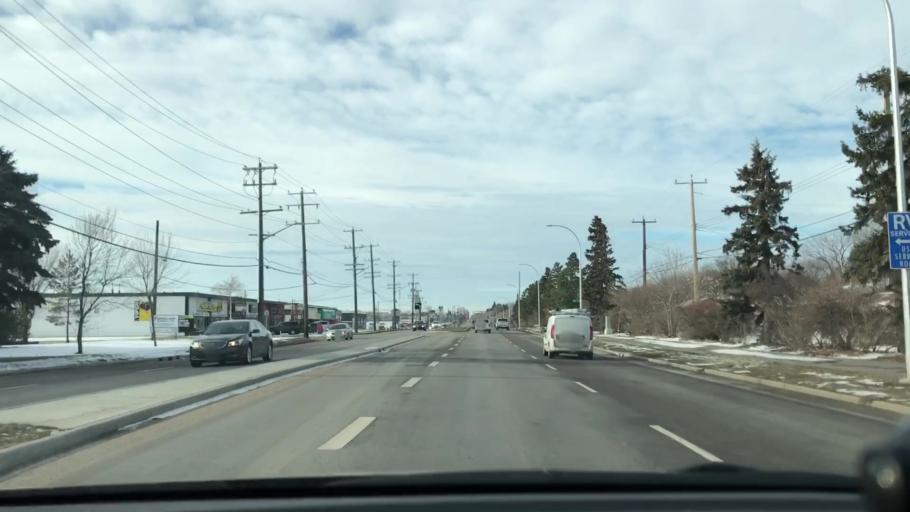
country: CA
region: Alberta
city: Edmonton
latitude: 53.4999
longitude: -113.4612
